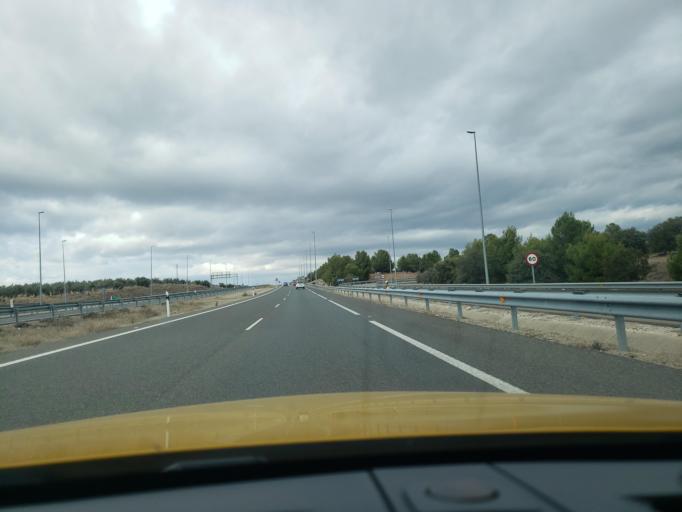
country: ES
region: Andalusia
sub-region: Provincia de Jaen
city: Jaen
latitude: 37.8189
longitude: -3.7656
